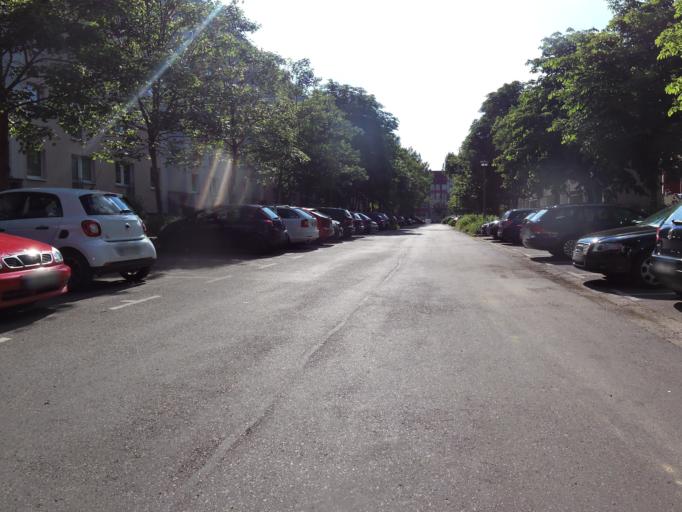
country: DE
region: Saxony
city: Leipzig
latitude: 51.3552
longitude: 12.4172
